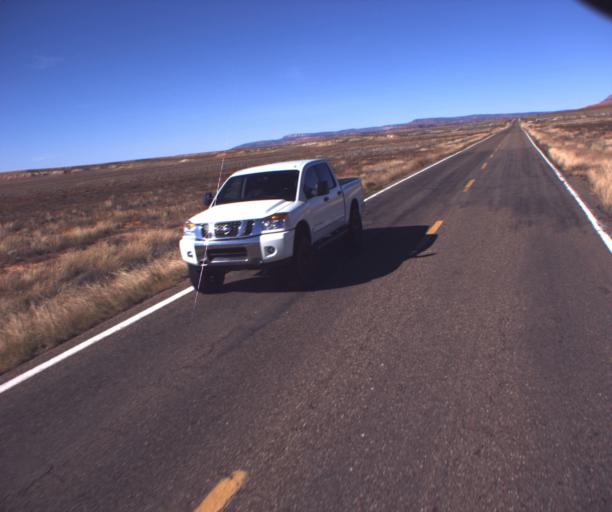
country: US
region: Arizona
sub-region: Coconino County
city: Fredonia
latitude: 36.9258
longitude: -112.4683
